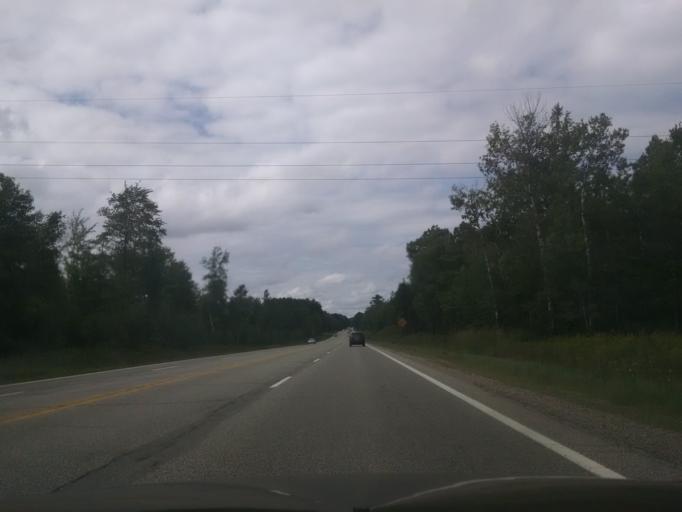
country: US
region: Michigan
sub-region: Osceola County
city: Evart
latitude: 44.0523
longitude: -85.1785
